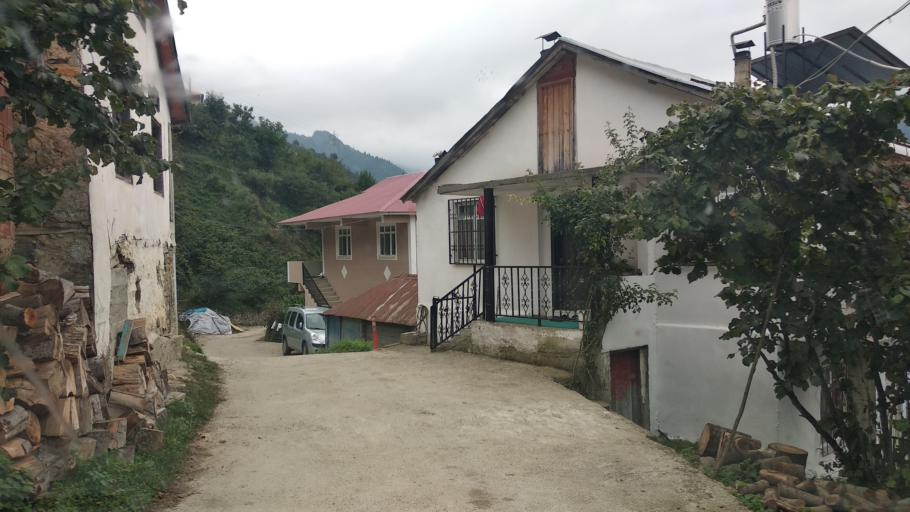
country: TR
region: Giresun
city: Dogankent
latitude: 40.7484
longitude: 38.9840
